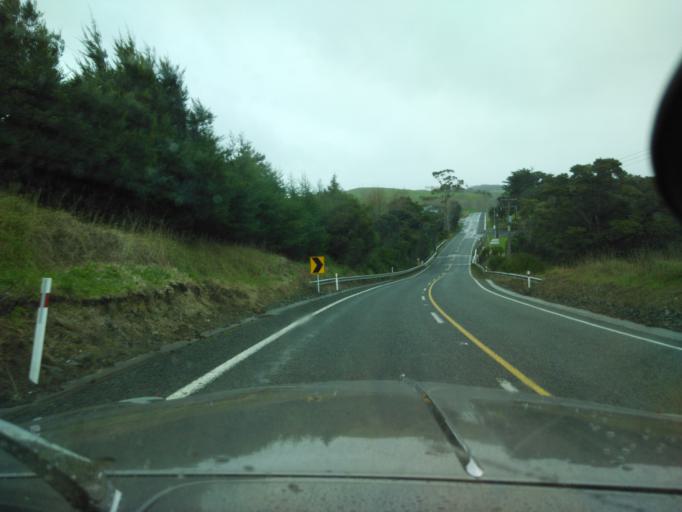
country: NZ
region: Auckland
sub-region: Auckland
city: Wellsford
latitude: -36.3750
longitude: 174.4542
